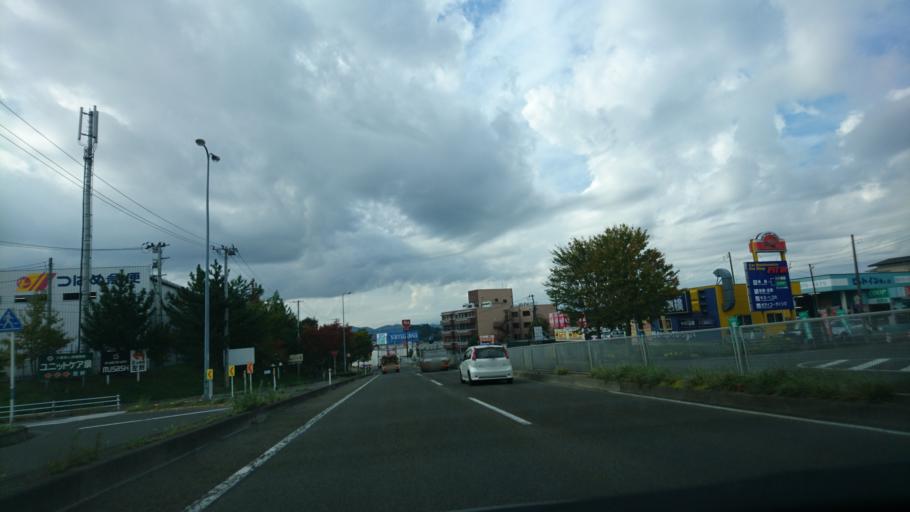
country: JP
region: Miyagi
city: Tomiya
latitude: 38.3581
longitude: 140.8726
